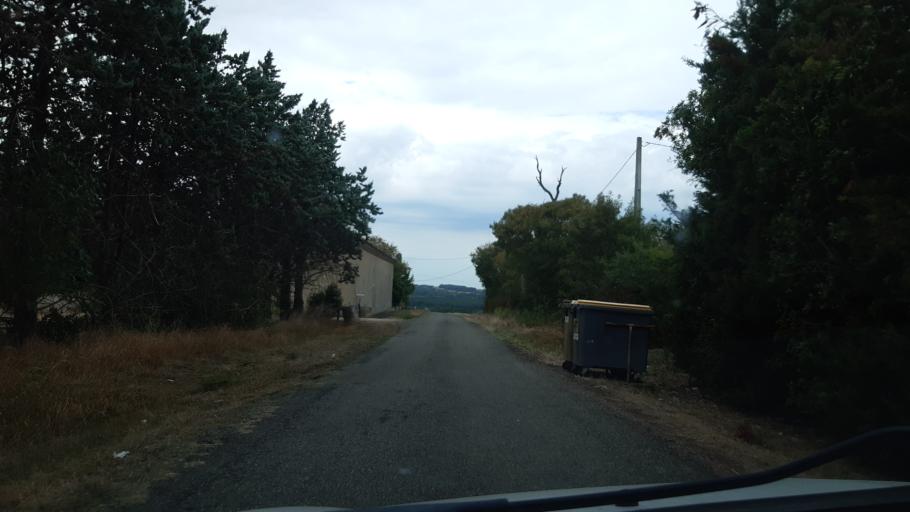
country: FR
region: Midi-Pyrenees
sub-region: Departement du Gers
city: Gimont
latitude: 43.7005
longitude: 0.9917
